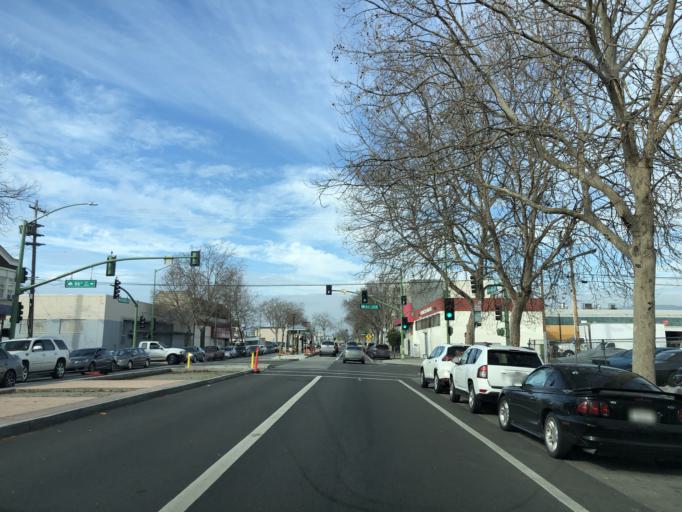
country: US
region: California
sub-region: Alameda County
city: San Leandro
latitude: 37.7454
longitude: -122.1713
